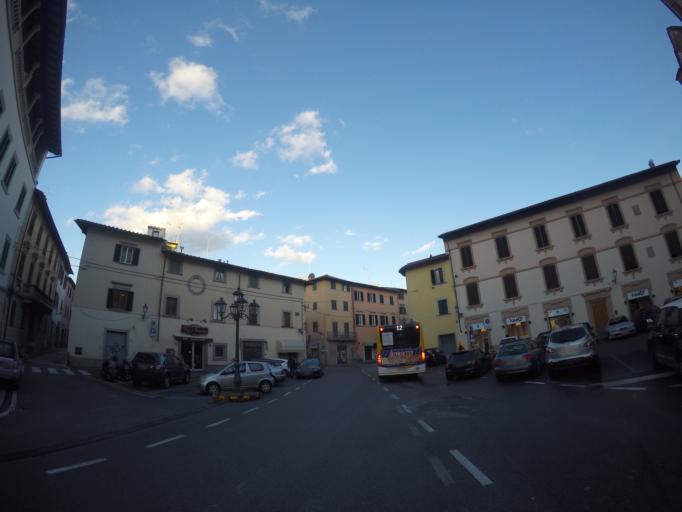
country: IT
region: Tuscany
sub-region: Provincia di Prato
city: Prato
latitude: 43.8817
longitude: 11.0942
